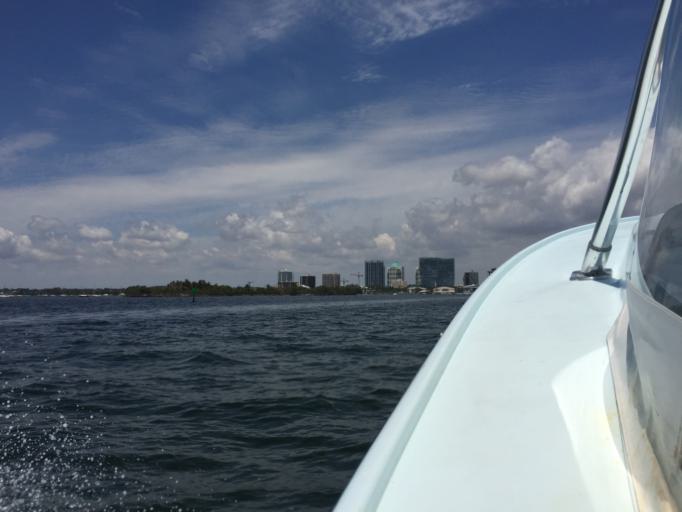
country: US
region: Florida
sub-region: Miami-Dade County
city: Coconut Grove
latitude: 25.7249
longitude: -80.2226
